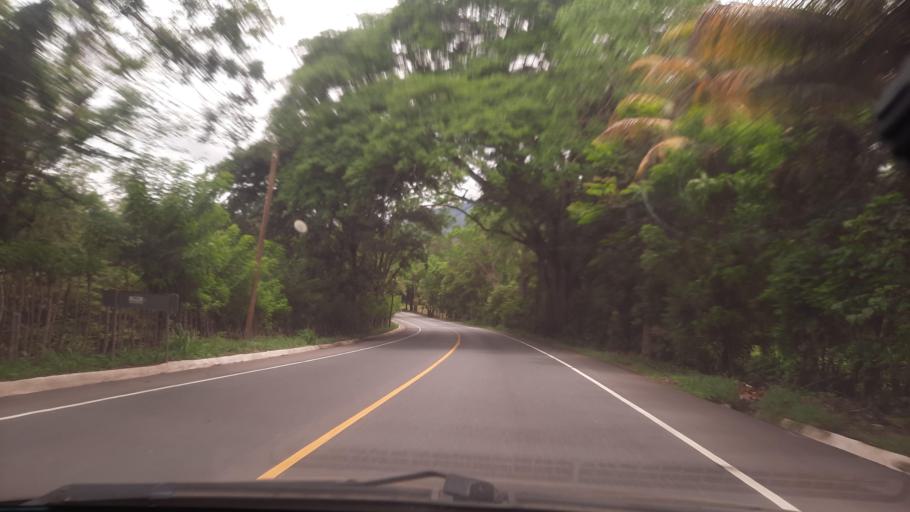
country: GT
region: Izabal
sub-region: Municipio de Los Amates
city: Los Amates
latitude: 15.2398
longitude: -89.1759
